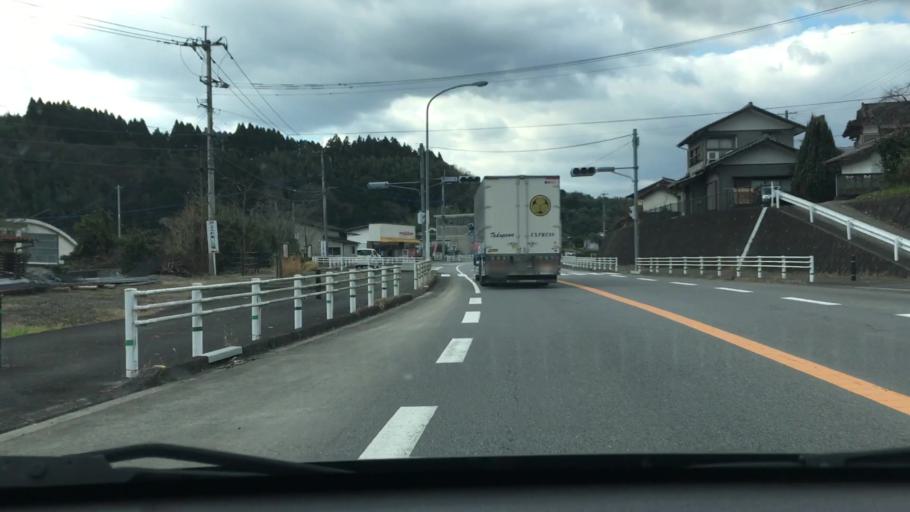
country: JP
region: Oita
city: Usuki
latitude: 33.0651
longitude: 131.6604
